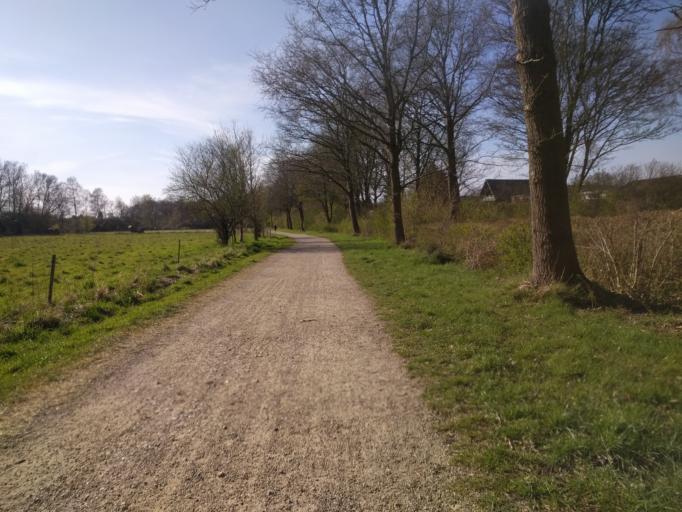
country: DK
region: South Denmark
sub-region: Odense Kommune
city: Seden
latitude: 55.3984
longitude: 10.4487
